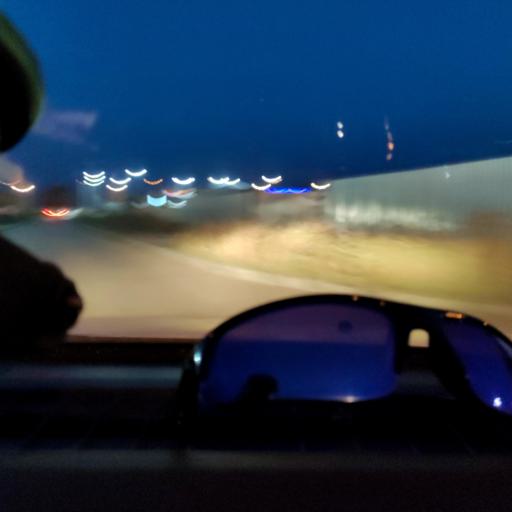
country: RU
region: Samara
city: Samara
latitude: 53.1141
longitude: 50.1624
